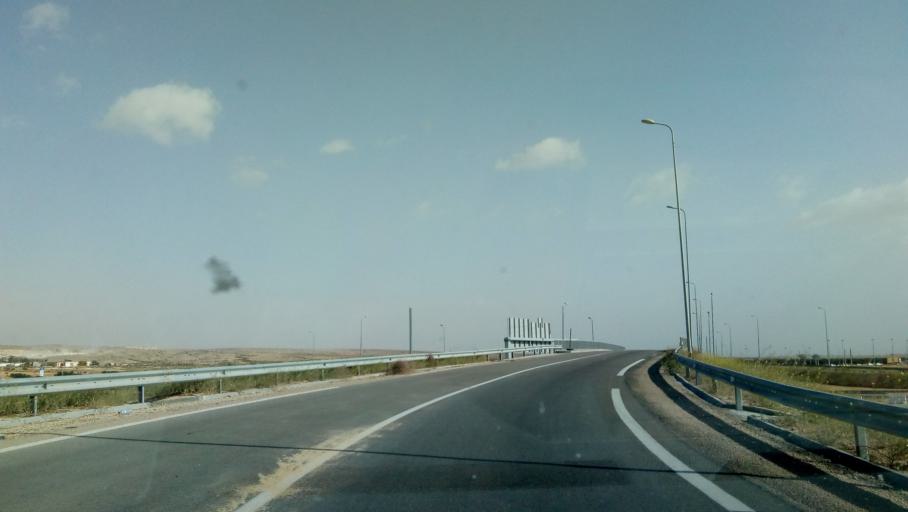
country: TN
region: Qabis
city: Gabes
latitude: 33.8806
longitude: 9.9956
